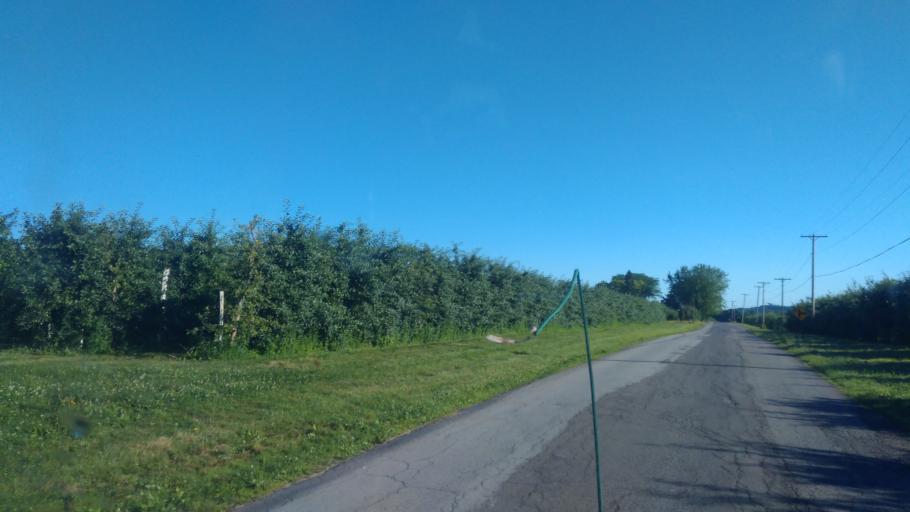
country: US
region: New York
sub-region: Wayne County
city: Sodus
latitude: 43.1796
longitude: -77.0617
